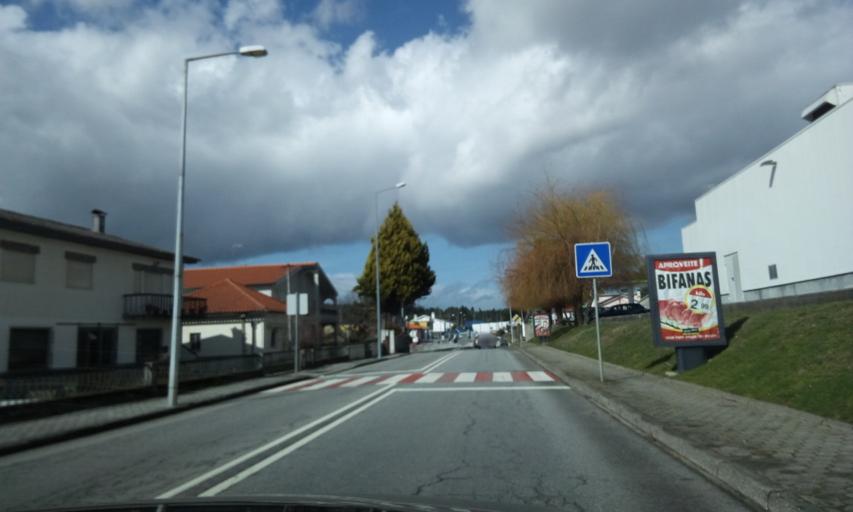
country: PT
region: Viseu
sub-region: Mangualde
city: Mangualde
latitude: 40.6149
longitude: -7.7595
